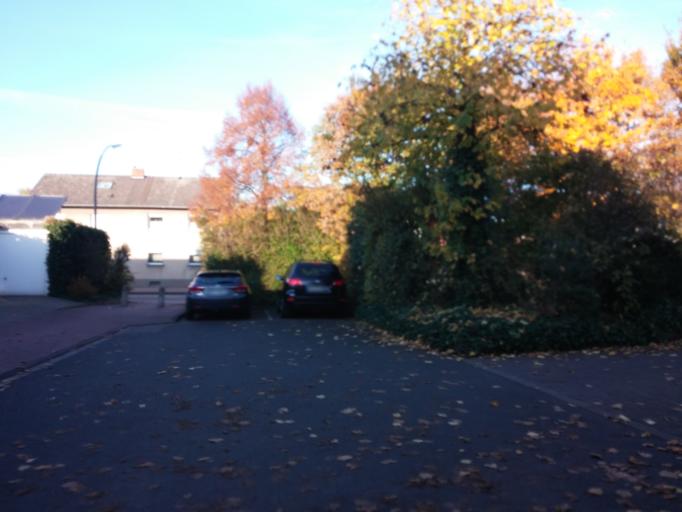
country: DE
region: North Rhine-Westphalia
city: Dorsten
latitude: 51.6573
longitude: 6.9832
